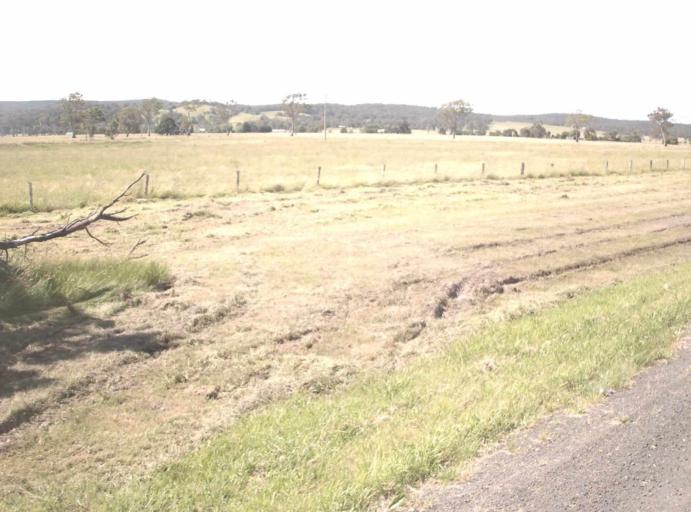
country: AU
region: Victoria
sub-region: Latrobe
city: Traralgon
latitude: -38.1437
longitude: 146.5265
